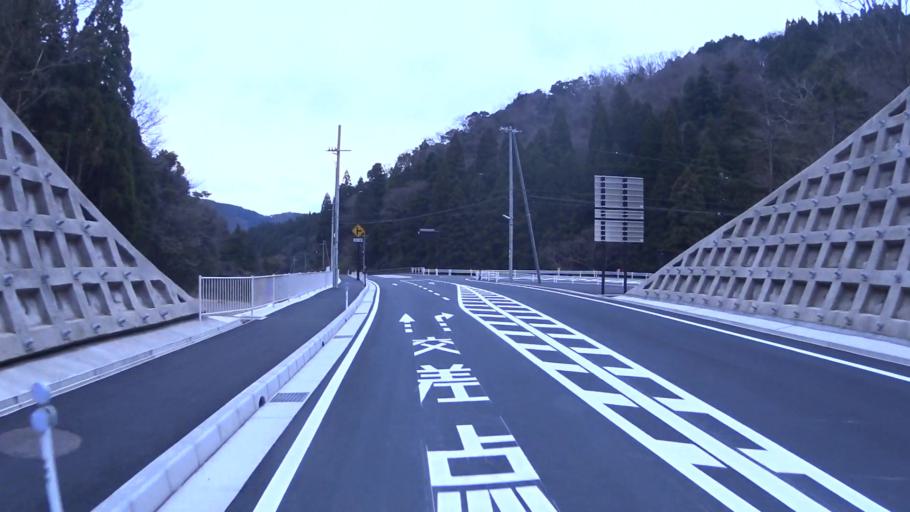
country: JP
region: Kyoto
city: Miyazu
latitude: 35.7382
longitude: 135.2546
